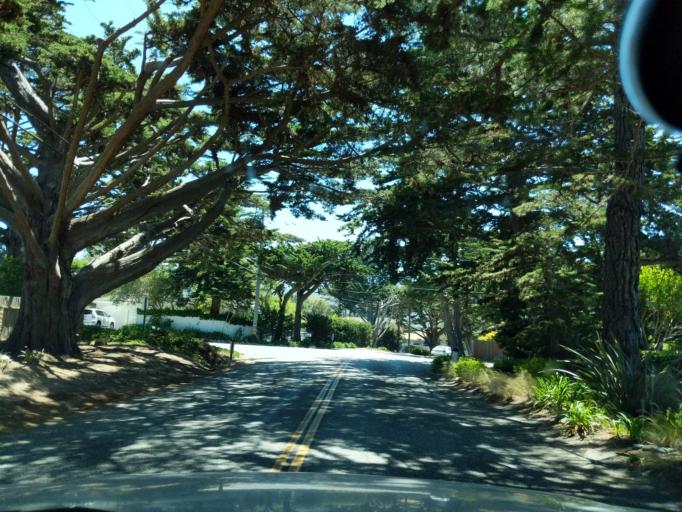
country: US
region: California
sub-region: Monterey County
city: Carmel-by-the-Sea
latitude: 36.5432
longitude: -121.9131
